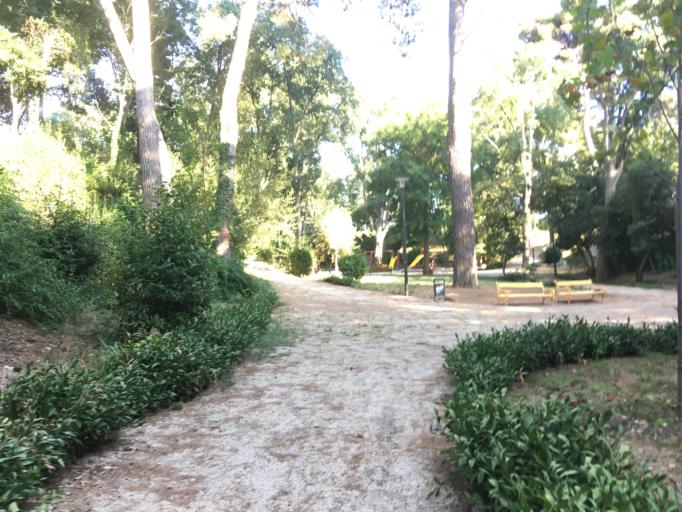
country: HR
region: Zadarska
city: Zadar
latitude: 44.1119
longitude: 15.2315
